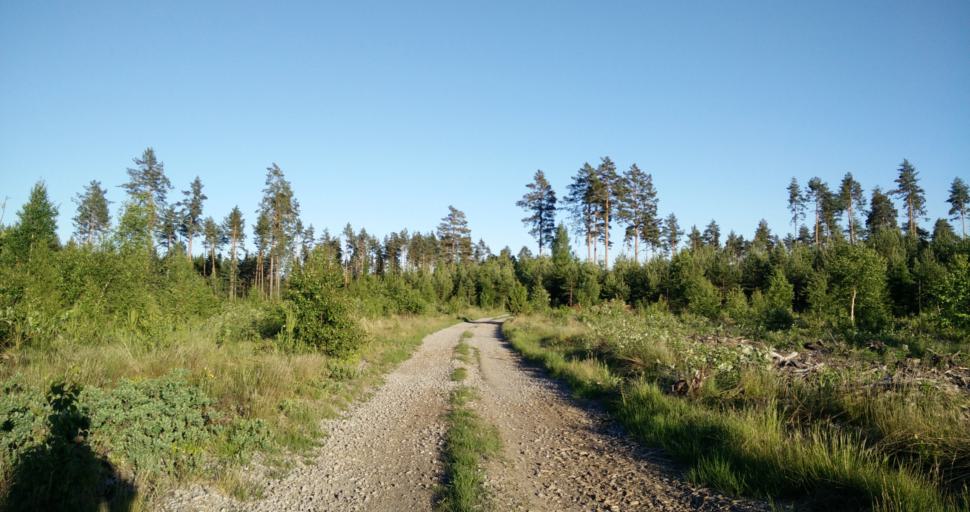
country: SE
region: Vaermland
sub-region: Hagfors Kommun
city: Hagfors
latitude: 60.0228
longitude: 13.5882
